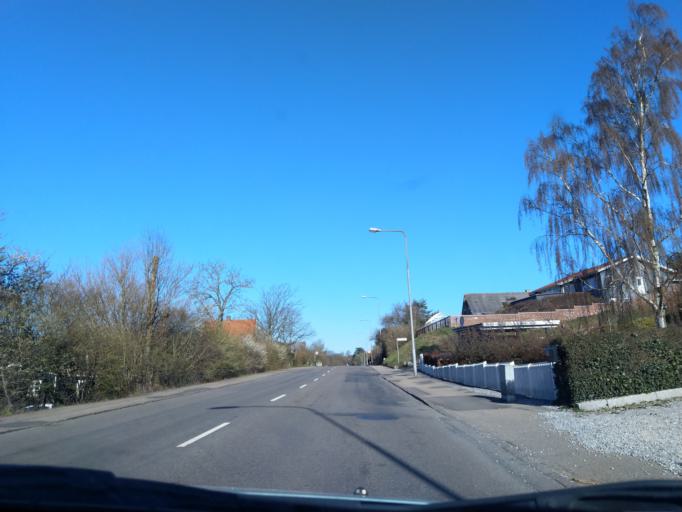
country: DK
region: Zealand
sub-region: Kalundborg Kommune
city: Kalundborg
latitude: 55.6964
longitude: 11.0431
